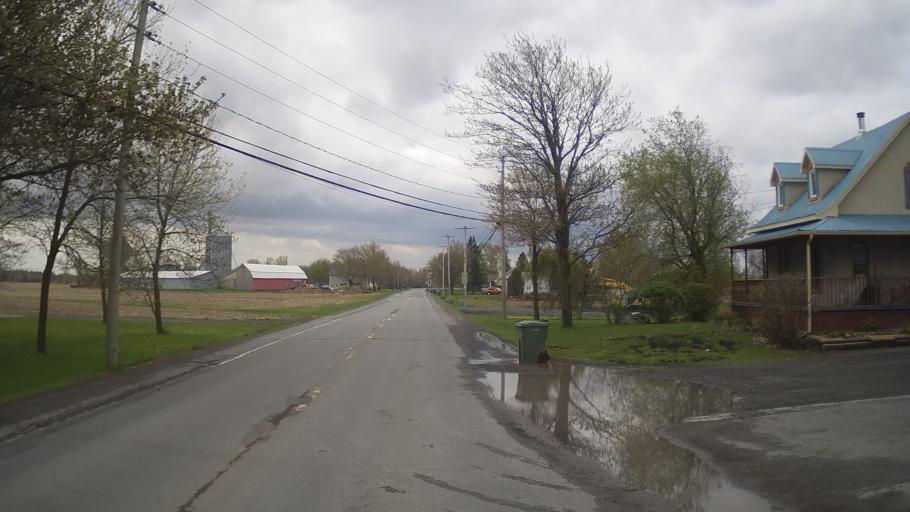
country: CA
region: Quebec
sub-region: Monteregie
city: Saint-Jean-sur-Richelieu
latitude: 45.3216
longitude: -73.1868
